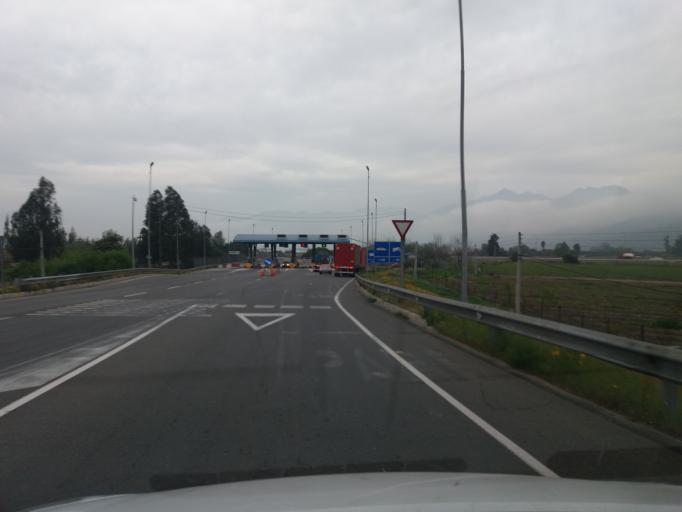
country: CL
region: Valparaiso
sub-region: Provincia de Quillota
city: Quillota
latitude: -32.9278
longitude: -71.2882
